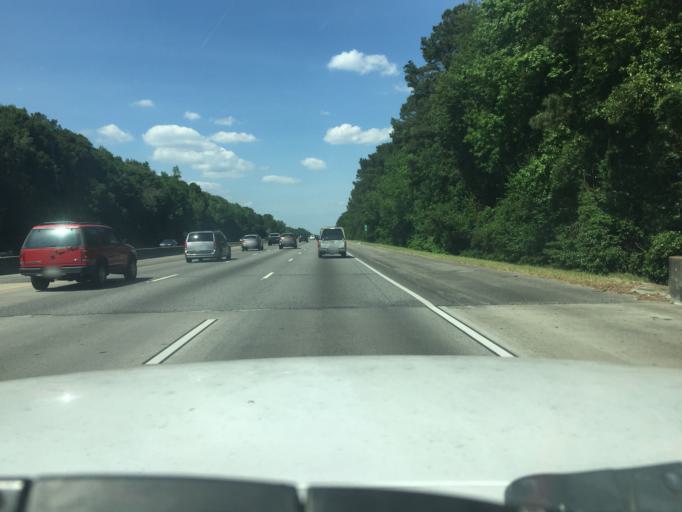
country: US
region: Georgia
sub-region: Chatham County
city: Georgetown
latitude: 32.0315
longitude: -81.2674
